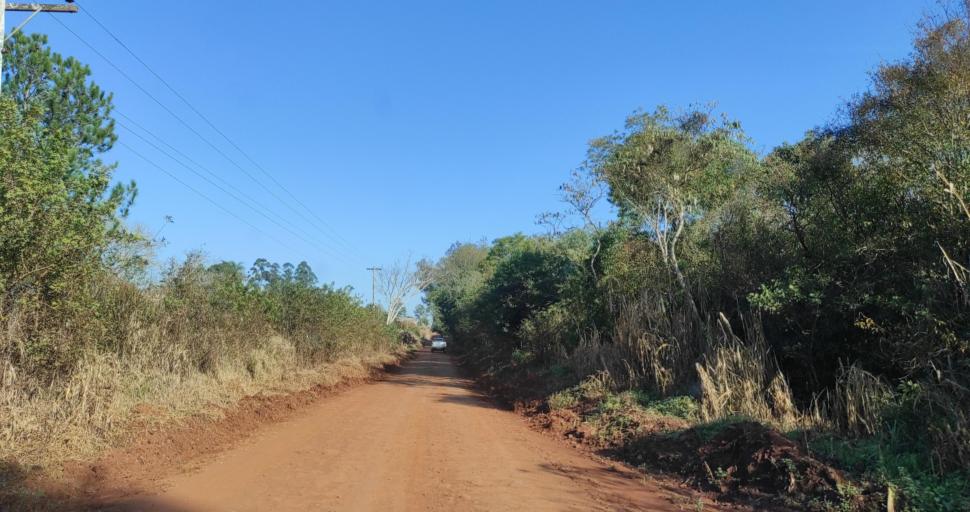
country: AR
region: Misiones
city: Capiovi
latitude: -26.8645
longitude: -55.0396
